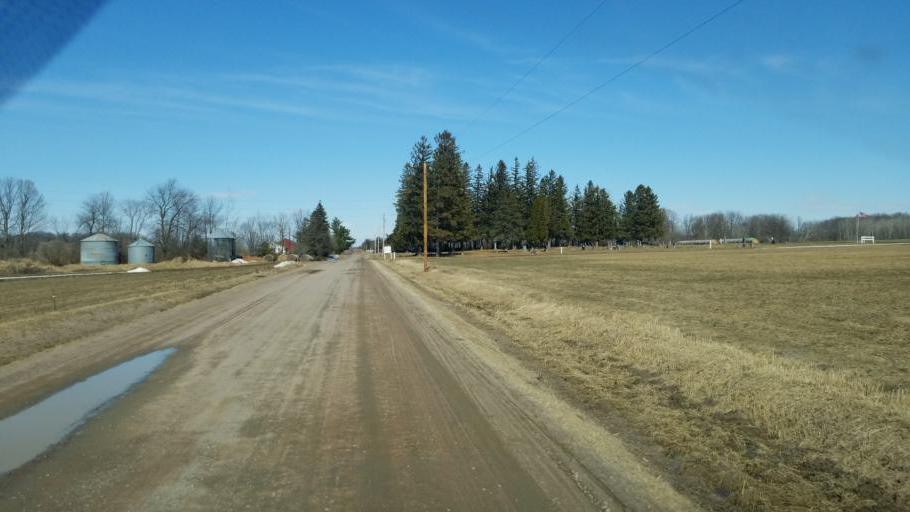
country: US
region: Wisconsin
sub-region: Marathon County
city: Spencer
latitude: 44.6170
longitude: -90.3767
